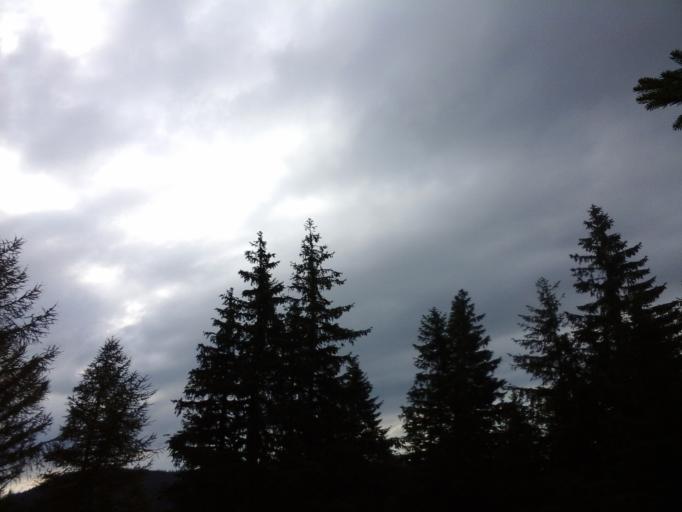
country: PL
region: Lesser Poland Voivodeship
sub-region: Powiat tatrzanski
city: Zakopane
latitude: 49.2651
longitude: 19.9858
